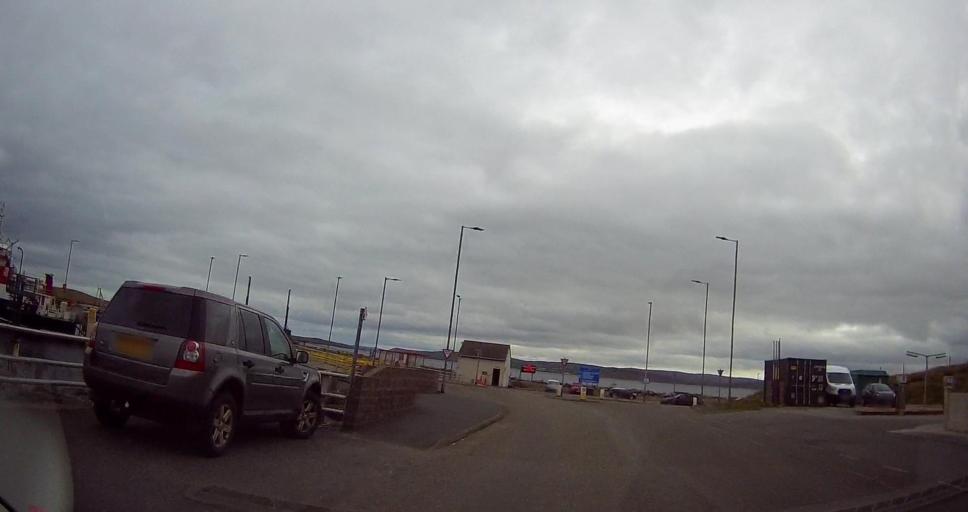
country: GB
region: Scotland
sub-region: Shetland Islands
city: Shetland
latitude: 60.4971
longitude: -1.1586
